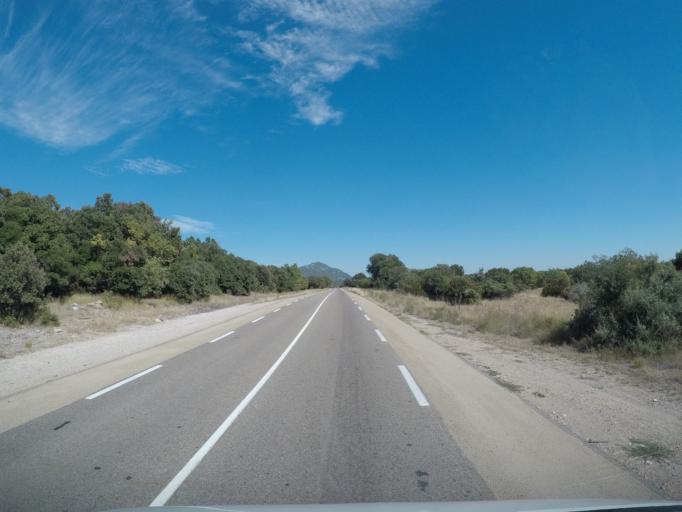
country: FR
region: Languedoc-Roussillon
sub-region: Departement de l'Herault
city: Saint-Martin-de-Londres
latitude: 43.7523
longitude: 3.7322
